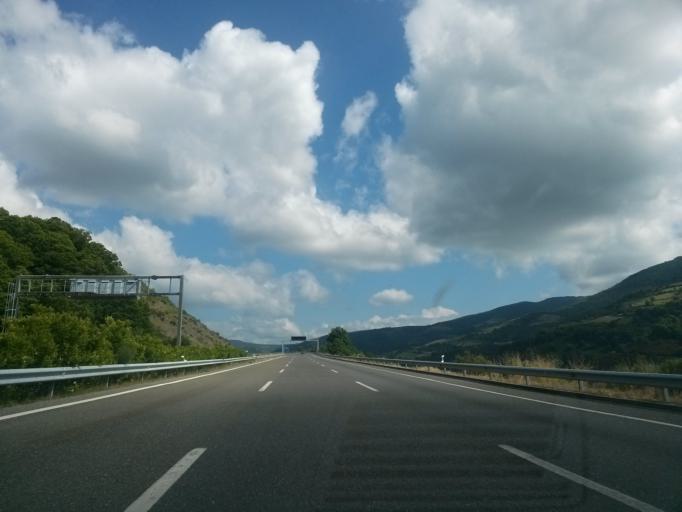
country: ES
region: Galicia
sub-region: Provincia de Lugo
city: San Roman
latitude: 42.7774
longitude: -7.0981
